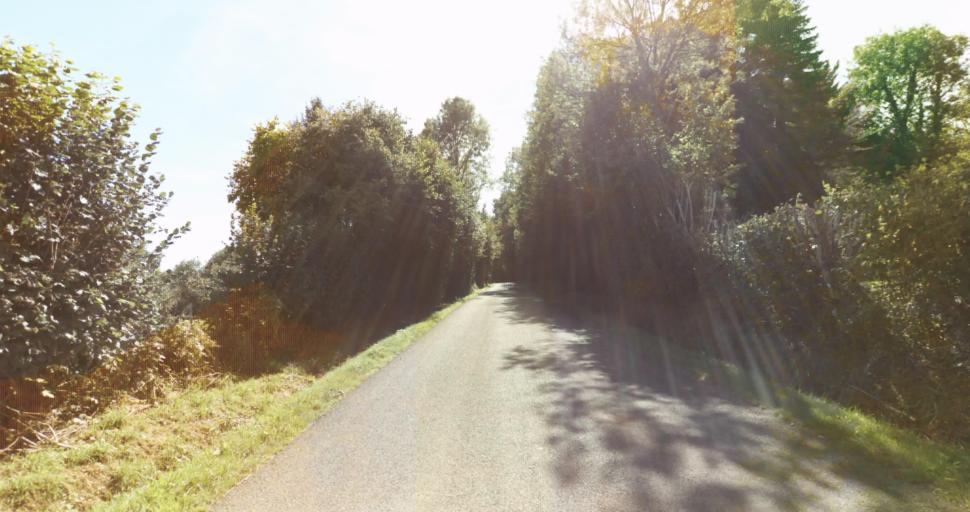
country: FR
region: Lower Normandy
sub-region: Departement de l'Orne
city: Gace
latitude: 48.7645
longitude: 0.2539
